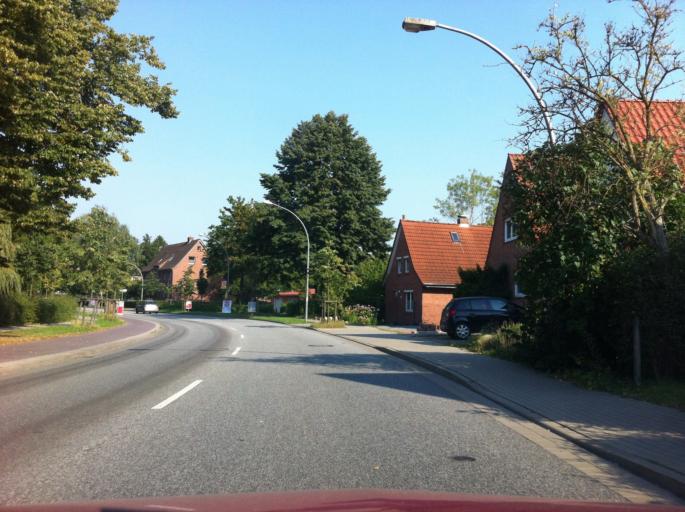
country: DE
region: Schleswig-Holstein
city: Oldenburg in Holstein
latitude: 54.2900
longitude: 10.8939
